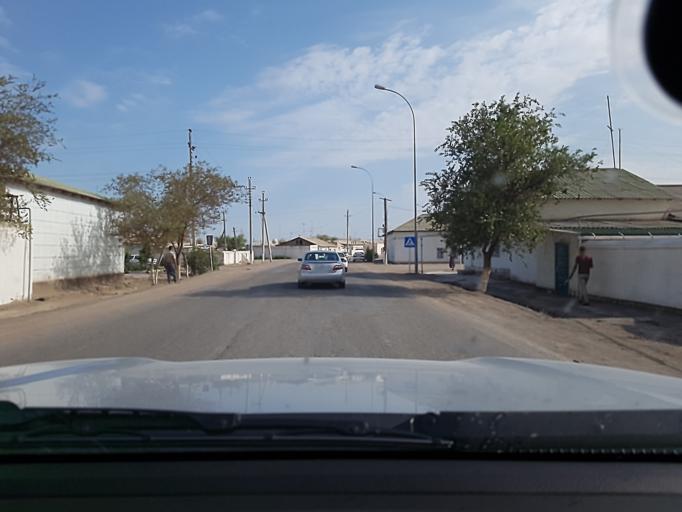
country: TM
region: Dasoguz
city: Koeneuergench
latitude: 42.3246
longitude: 59.1599
